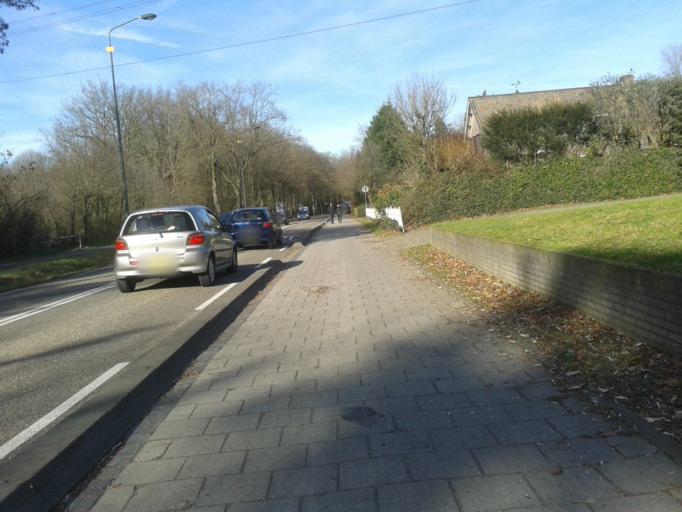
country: NL
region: North Brabant
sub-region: Gemeente Oisterwijk
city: Oisterwijk
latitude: 51.5519
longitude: 5.1743
